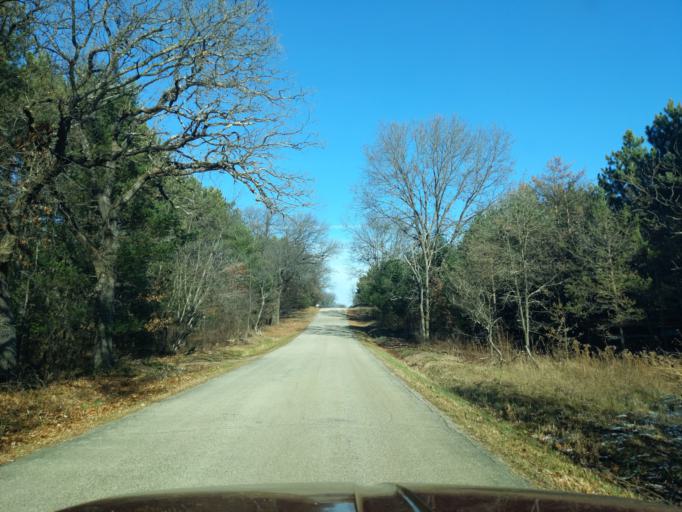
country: US
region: Wisconsin
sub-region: Waushara County
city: Silver Lake
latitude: 44.1074
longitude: -89.1689
